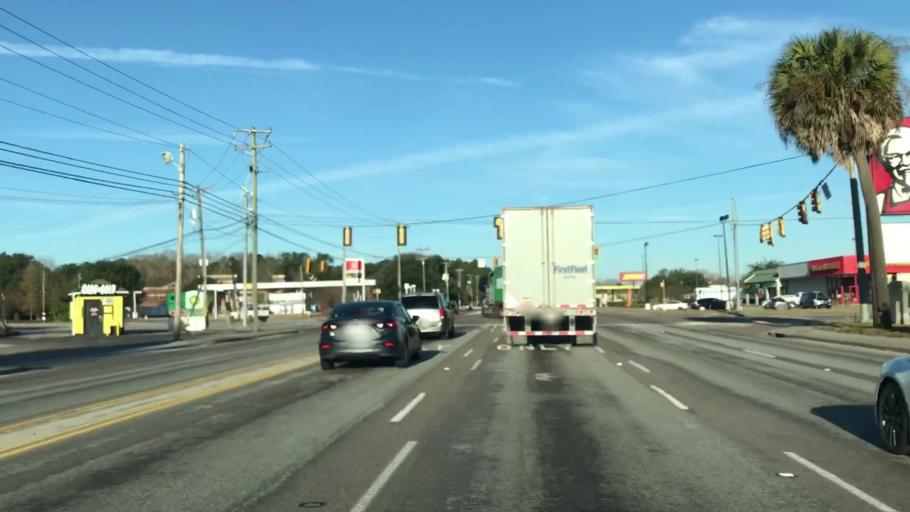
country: US
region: South Carolina
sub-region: Berkeley County
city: Ladson
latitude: 32.9878
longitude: -80.0977
